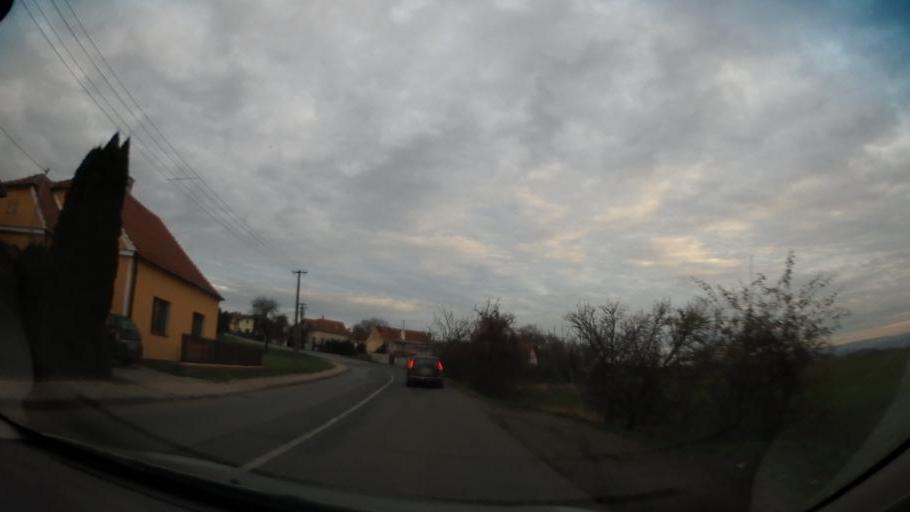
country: CZ
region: South Moravian
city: Oslavany
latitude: 49.1326
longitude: 16.3524
